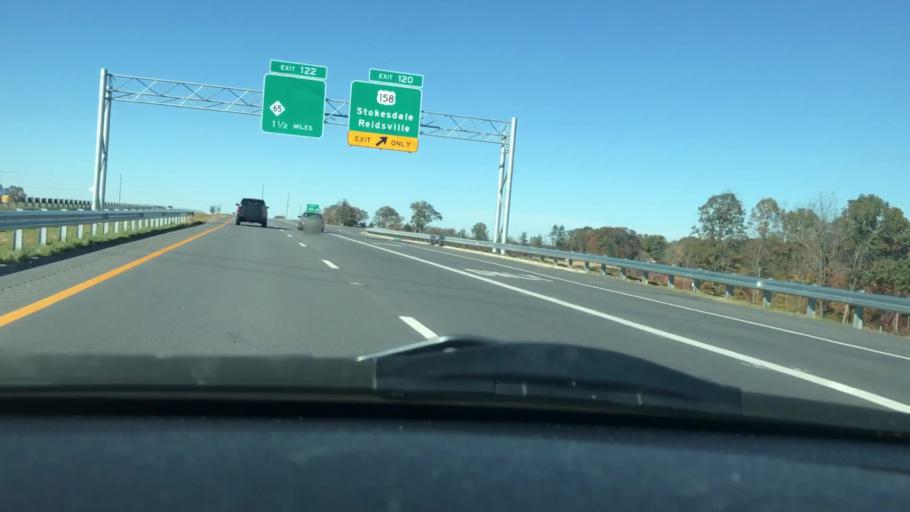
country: US
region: North Carolina
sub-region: Guilford County
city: Summerfield
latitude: 36.2431
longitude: -79.9196
